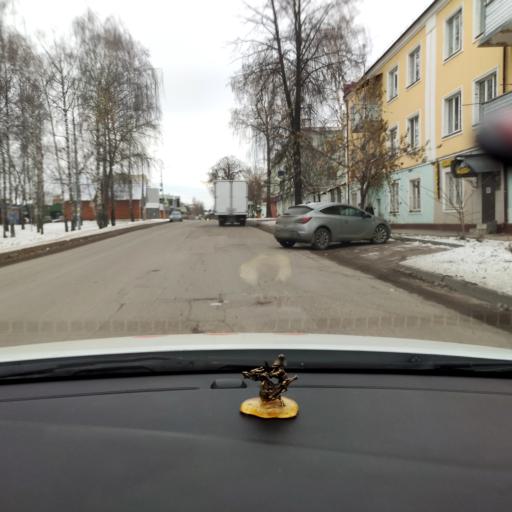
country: RU
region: Tatarstan
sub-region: Zelenodol'skiy Rayon
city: Zelenodolsk
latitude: 55.8506
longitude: 48.5039
